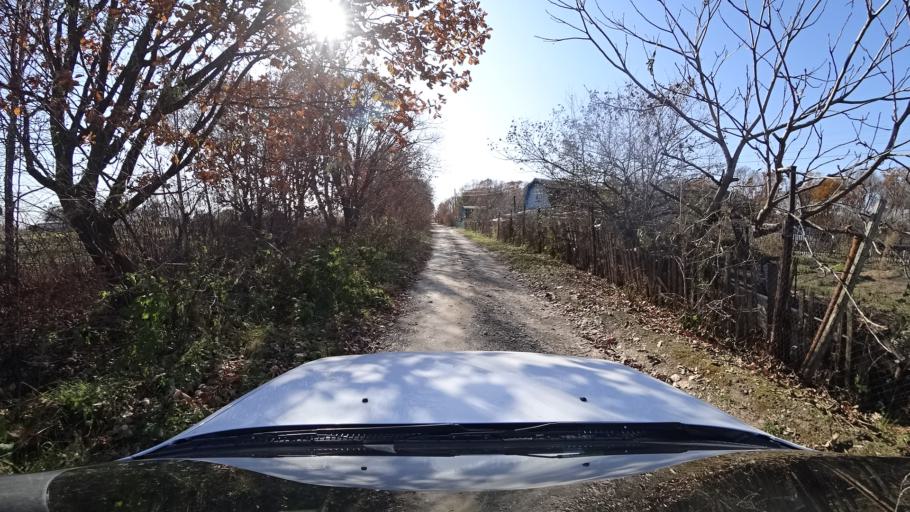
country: RU
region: Primorskiy
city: Dal'nerechensk
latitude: 45.8847
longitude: 133.7410
